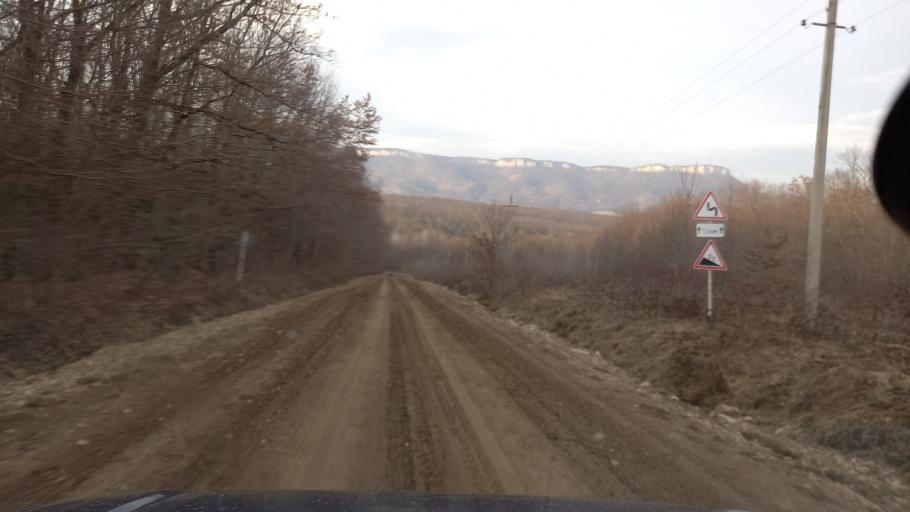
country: RU
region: Adygeya
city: Kamennomostskiy
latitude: 44.1894
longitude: 40.2612
